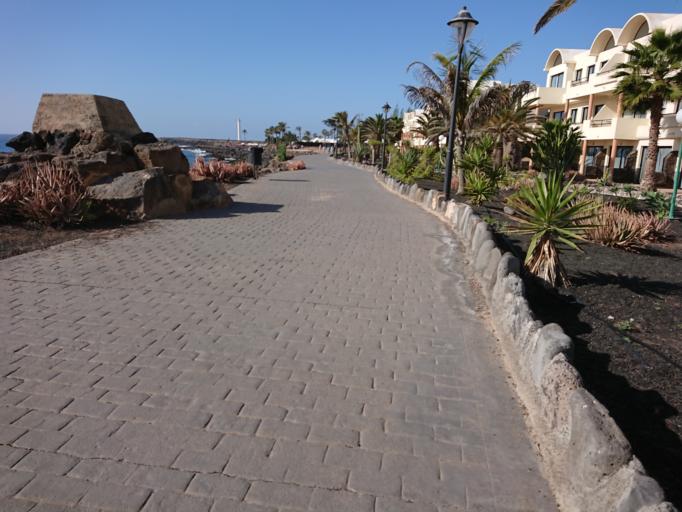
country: ES
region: Canary Islands
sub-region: Provincia de Las Palmas
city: Playa Blanca
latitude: 28.8612
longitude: -13.8621
